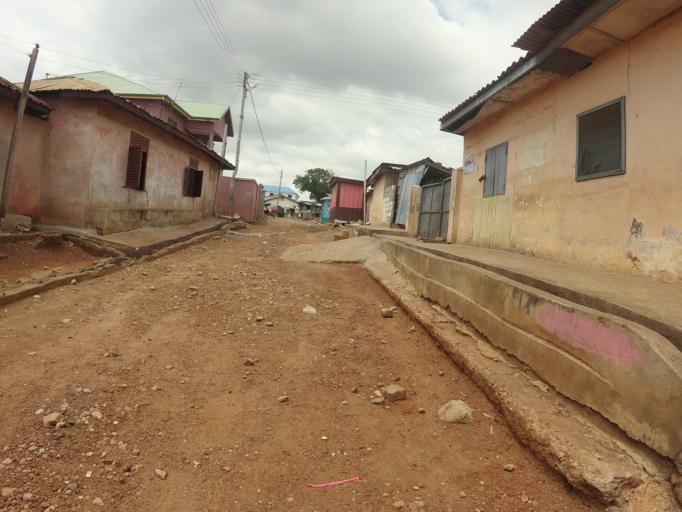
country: GH
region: Greater Accra
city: Accra
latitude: 5.5864
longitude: -0.2041
